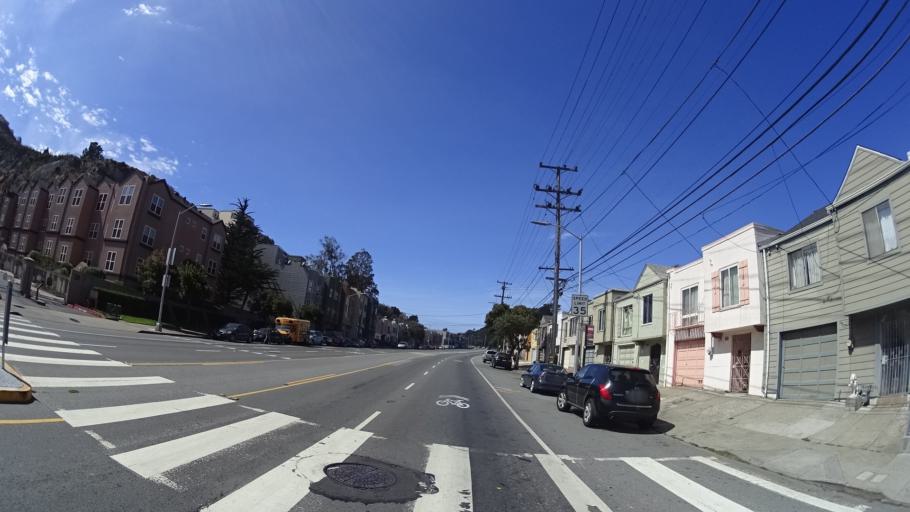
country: US
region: California
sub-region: San Mateo County
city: Daly City
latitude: 37.7109
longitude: -122.4259
